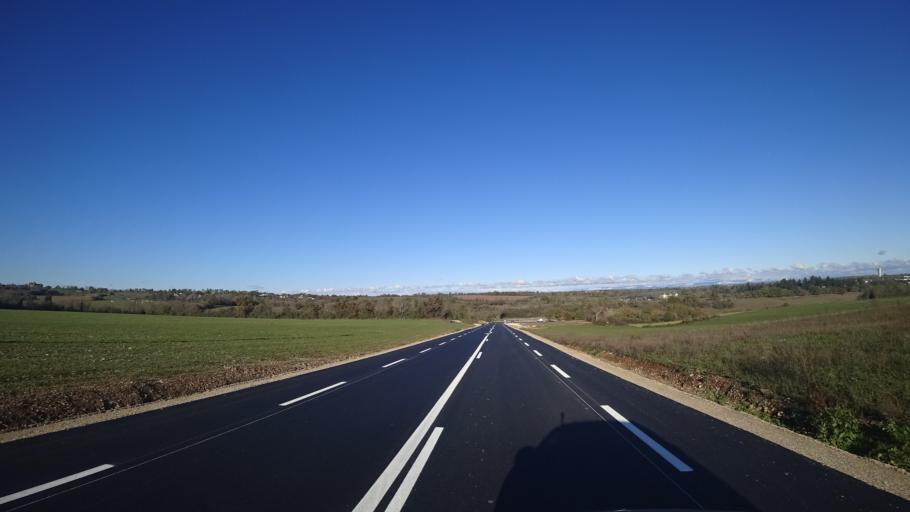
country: FR
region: Midi-Pyrenees
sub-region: Departement de l'Aveyron
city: Olemps
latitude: 44.3782
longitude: 2.5523
